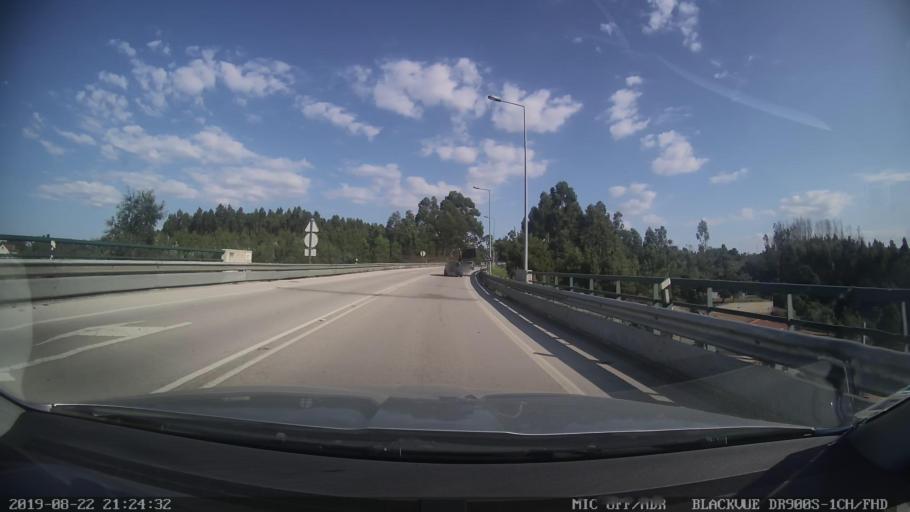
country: PT
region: Castelo Branco
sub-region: Serta
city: Serta
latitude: 39.8423
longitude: -8.1238
